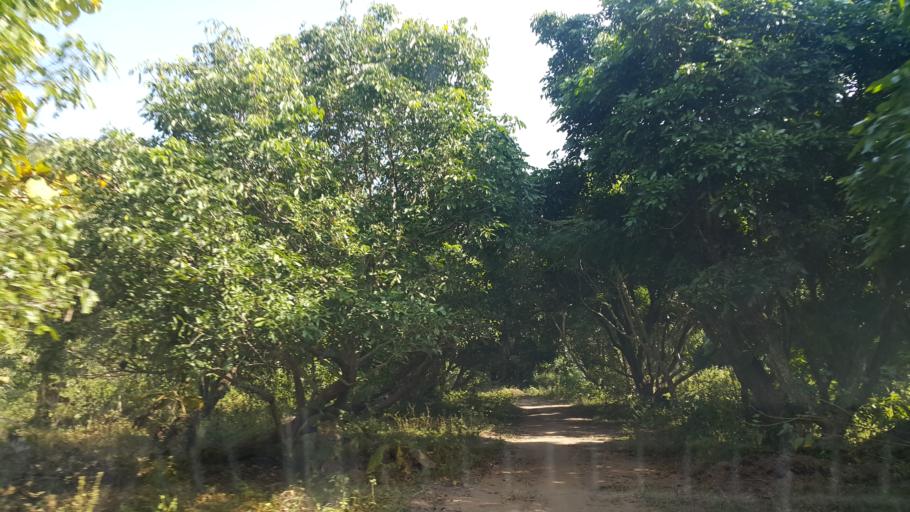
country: TH
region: Lamphun
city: Ban Thi
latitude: 18.5737
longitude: 99.1720
